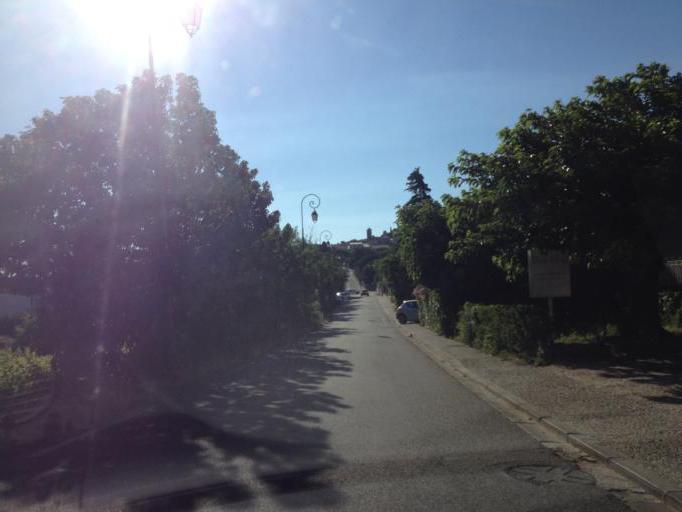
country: FR
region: Provence-Alpes-Cote d'Azur
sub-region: Departement du Vaucluse
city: Chateauneuf-du-Pape
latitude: 44.0545
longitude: 4.8373
